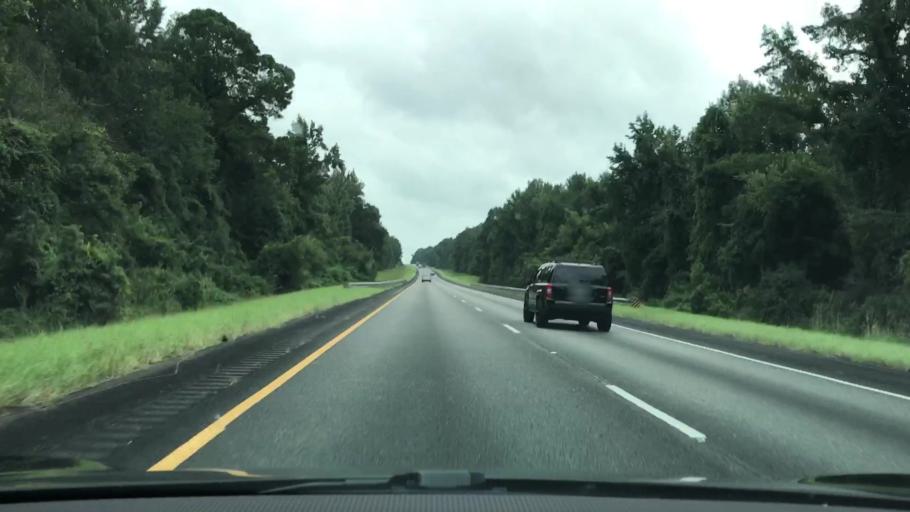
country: US
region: Alabama
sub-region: Elmore County
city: Tallassee
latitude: 32.4392
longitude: -85.8373
